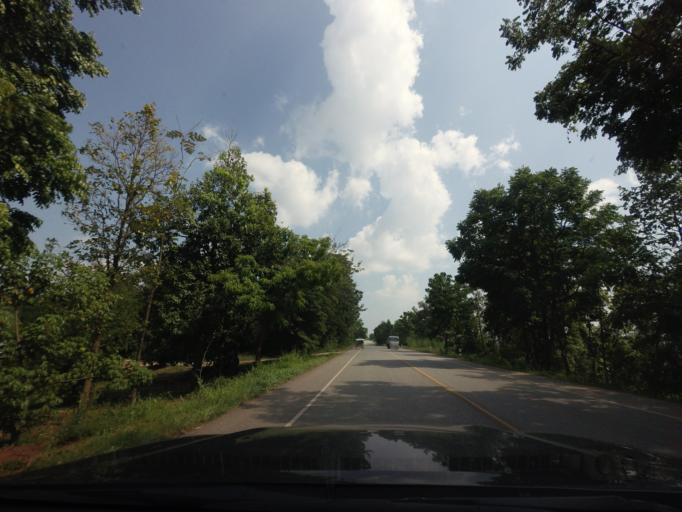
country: TH
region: Phitsanulok
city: Chat Trakan
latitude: 17.2680
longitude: 100.5479
